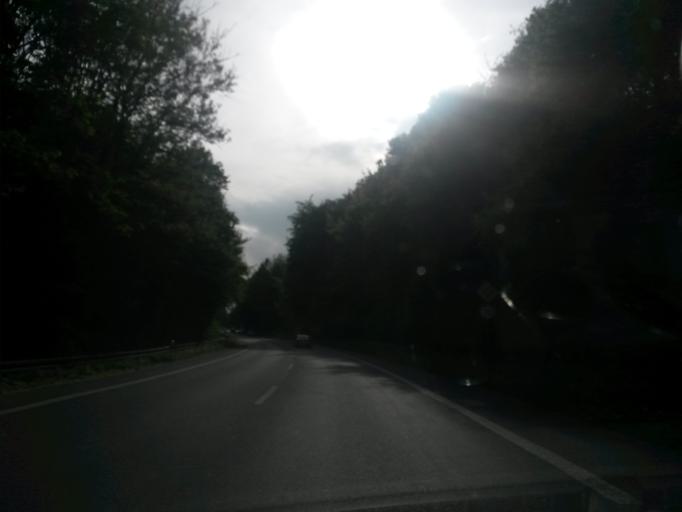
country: DE
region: North Rhine-Westphalia
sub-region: Regierungsbezirk Arnsberg
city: Hagen
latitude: 51.3509
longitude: 7.5368
